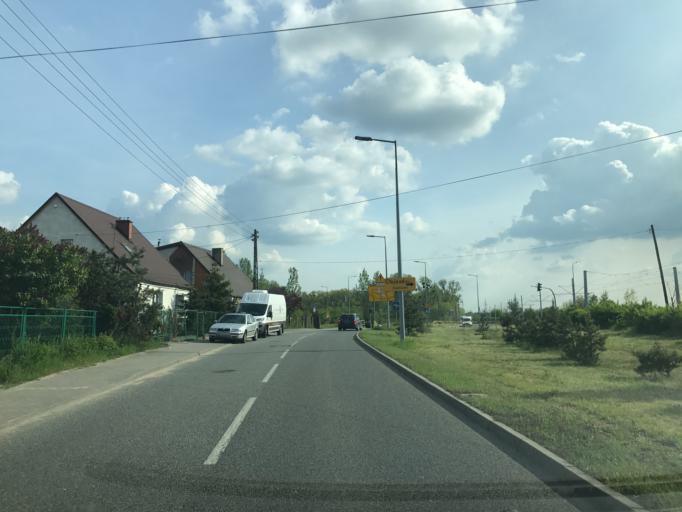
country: PL
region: Kujawsko-Pomorskie
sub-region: Bydgoszcz
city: Fordon
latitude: 53.1052
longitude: 18.1074
